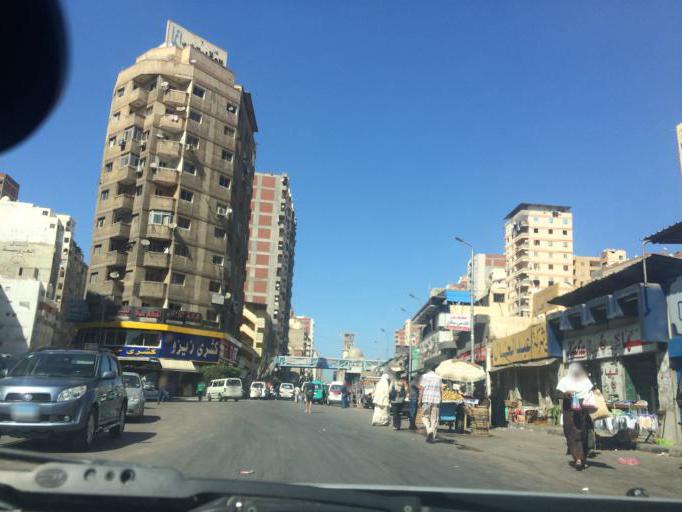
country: EG
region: Alexandria
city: Alexandria
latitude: 31.2488
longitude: 29.9801
